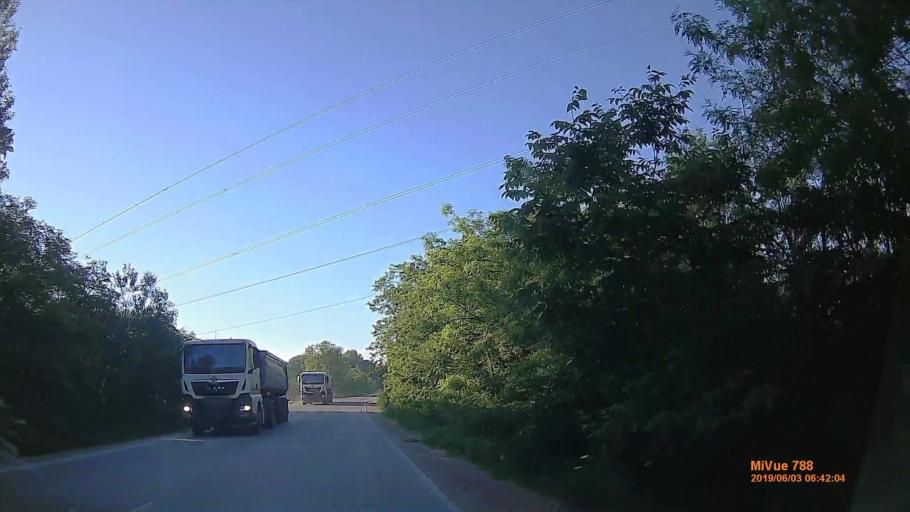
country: HU
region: Pest
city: Delegyhaza
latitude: 47.2700
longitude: 19.1110
